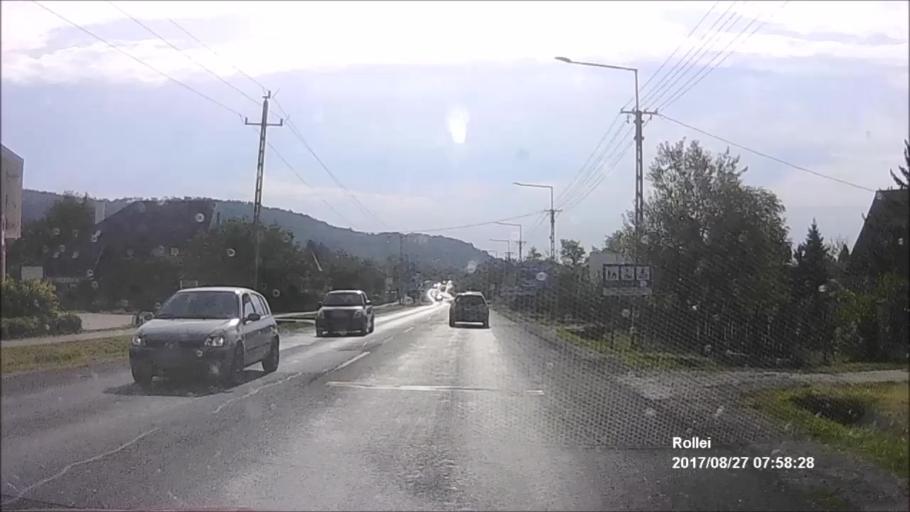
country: HU
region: Zala
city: Gyenesdias
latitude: 46.7725
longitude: 17.2860
